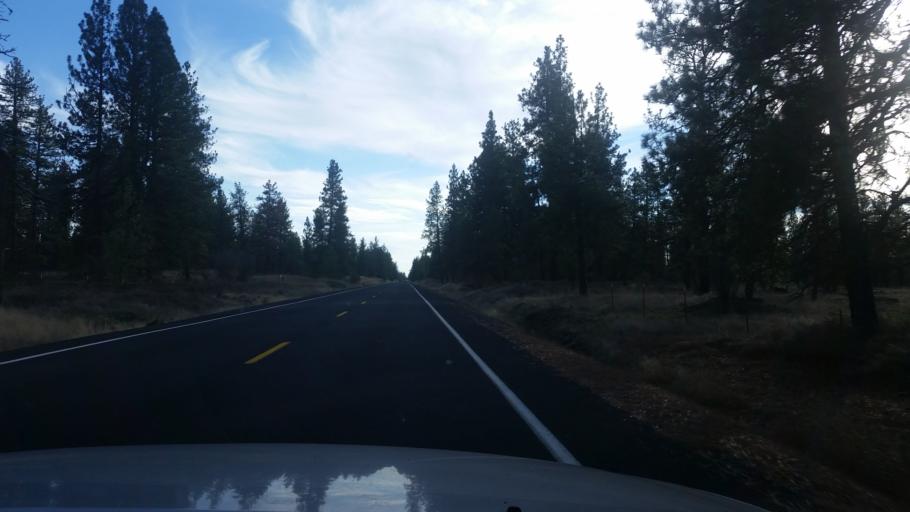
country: US
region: Washington
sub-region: Spokane County
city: Cheney
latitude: 47.4212
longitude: -117.5665
